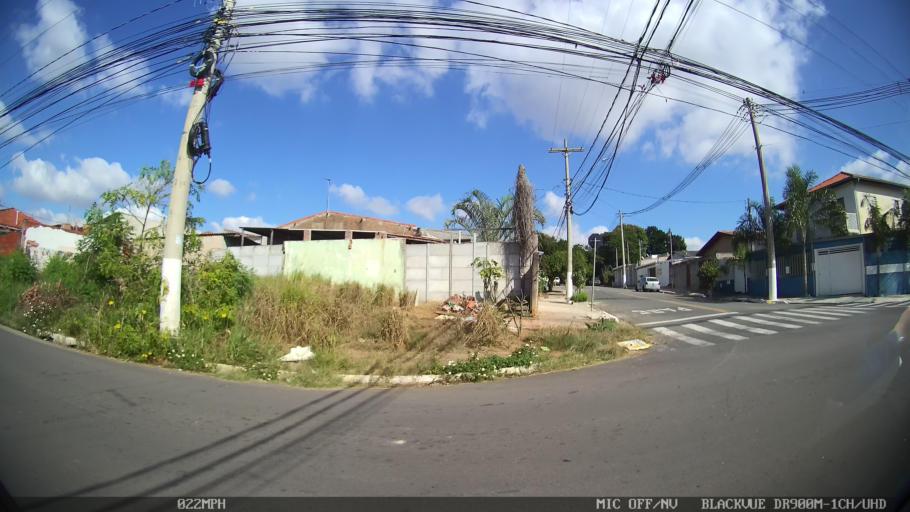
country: BR
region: Sao Paulo
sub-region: Hortolandia
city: Hortolandia
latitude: -22.8976
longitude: -47.1968
